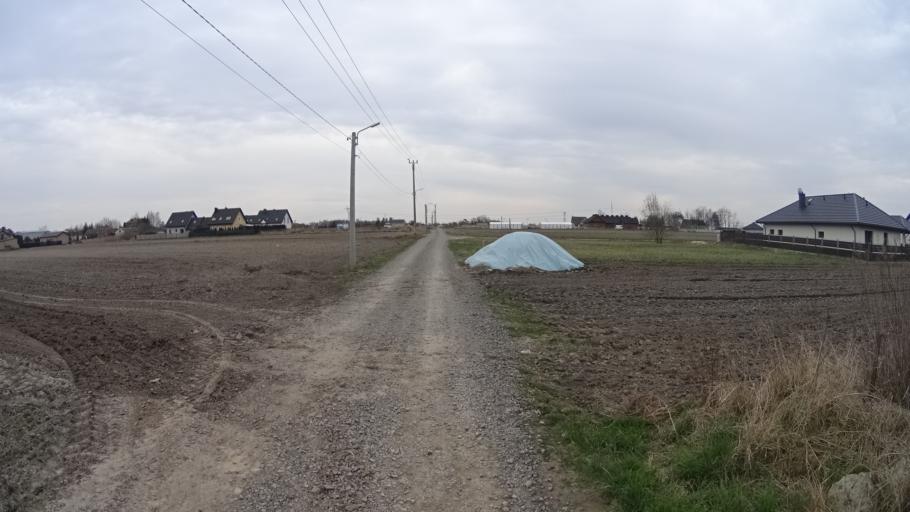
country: PL
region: Masovian Voivodeship
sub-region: Powiat warszawski zachodni
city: Jozefow
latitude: 52.2449
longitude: 20.6884
